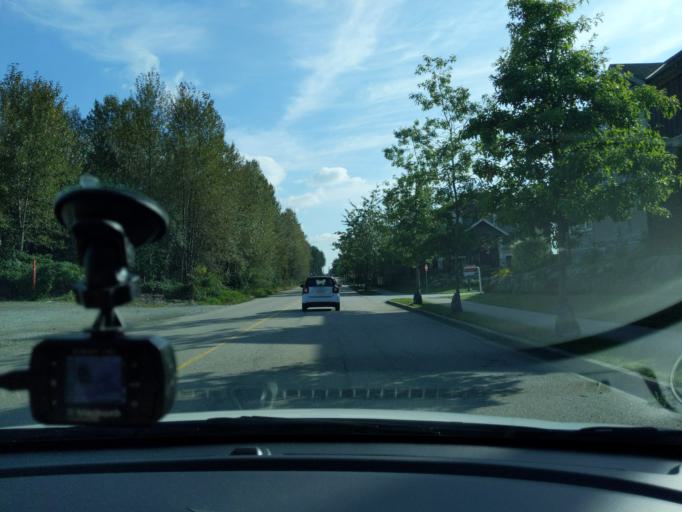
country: CA
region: British Columbia
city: Pitt Meadows
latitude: 49.2057
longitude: -122.6783
